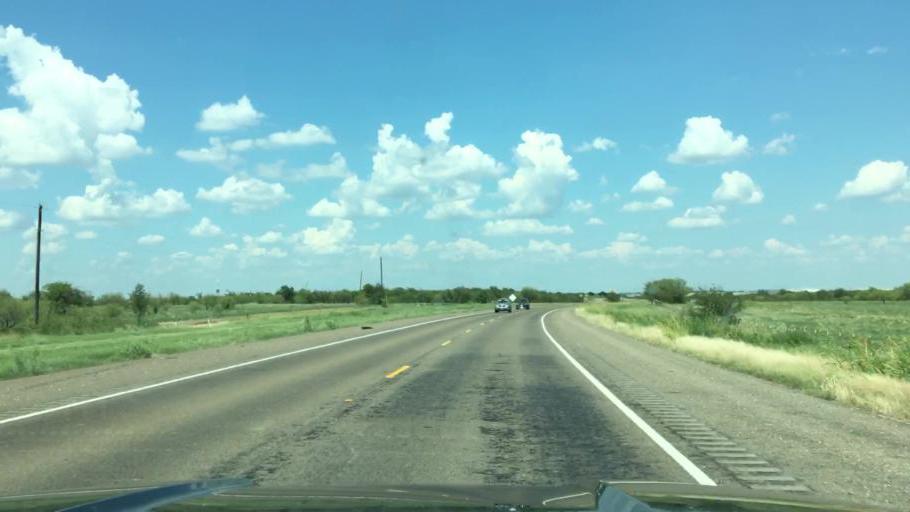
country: US
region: Texas
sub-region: Tarrant County
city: Haslet
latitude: 33.0091
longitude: -97.3404
